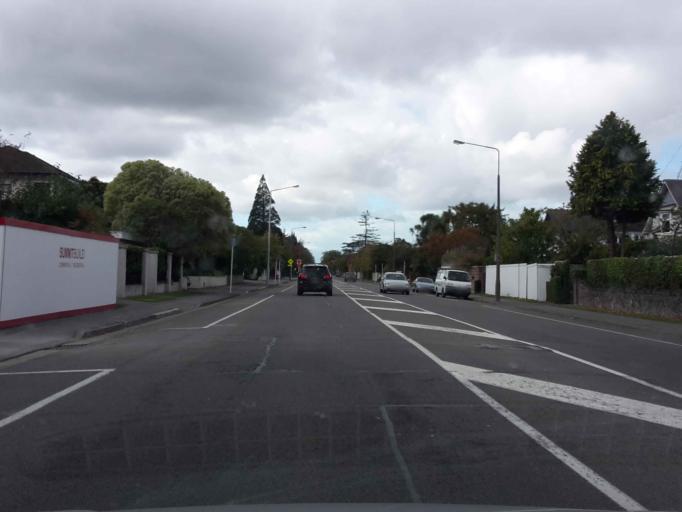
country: NZ
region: Canterbury
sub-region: Christchurch City
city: Christchurch
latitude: -43.5114
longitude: 172.6145
